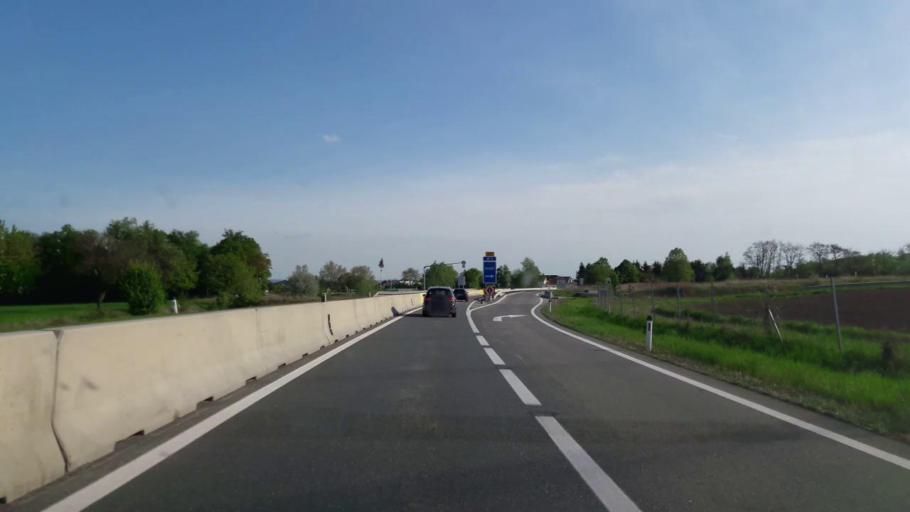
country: AT
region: Lower Austria
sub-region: Politischer Bezirk Korneuburg
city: Sierndorf
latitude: 48.4357
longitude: 16.1645
